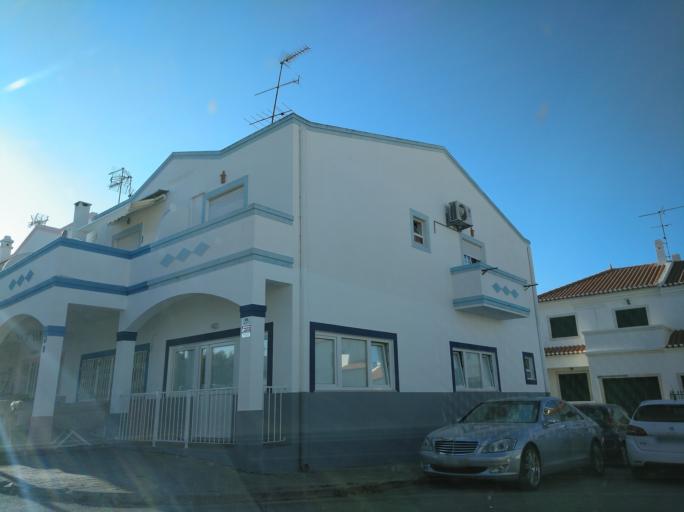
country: PT
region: Faro
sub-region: Vila Real de Santo Antonio
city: Monte Gordo
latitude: 37.1776
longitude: -7.4994
